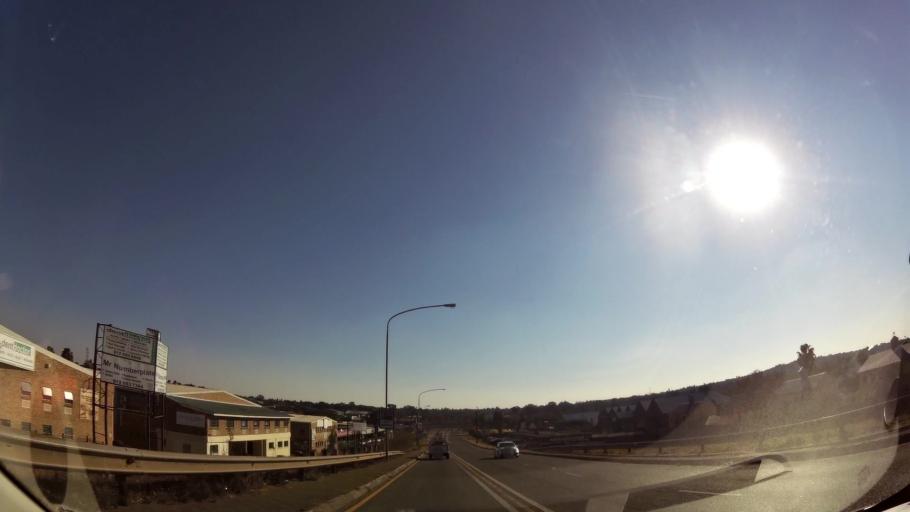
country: ZA
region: Gauteng
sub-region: City of Tshwane Metropolitan Municipality
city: Centurion
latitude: -25.8623
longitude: 28.1704
